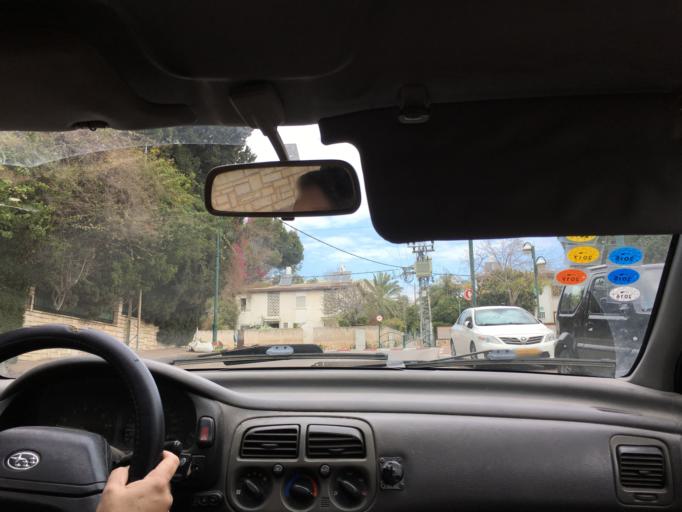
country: IL
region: Tel Aviv
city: Ramat HaSharon
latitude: 32.1352
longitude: 34.8506
